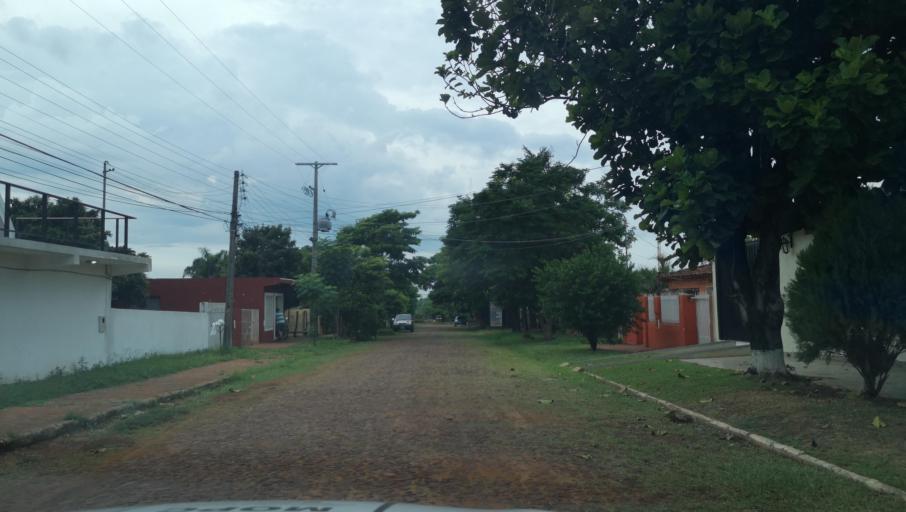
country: PY
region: Misiones
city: Santa Maria
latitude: -26.8865
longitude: -57.0382
